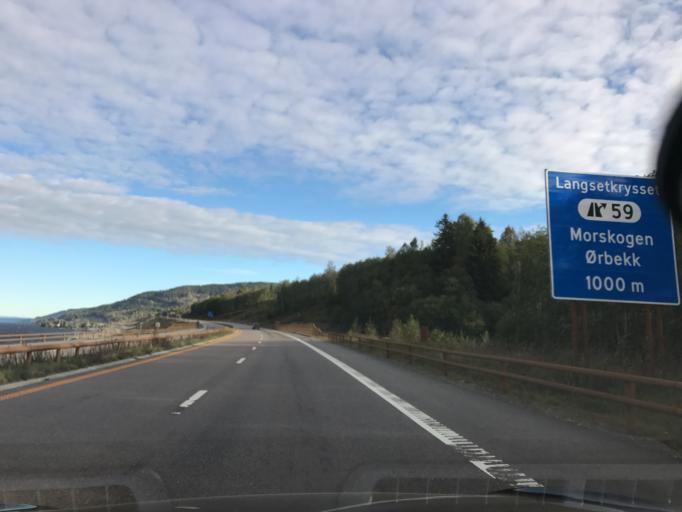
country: NO
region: Akershus
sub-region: Eidsvoll
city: Eidsvoll
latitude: 60.4015
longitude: 11.2355
